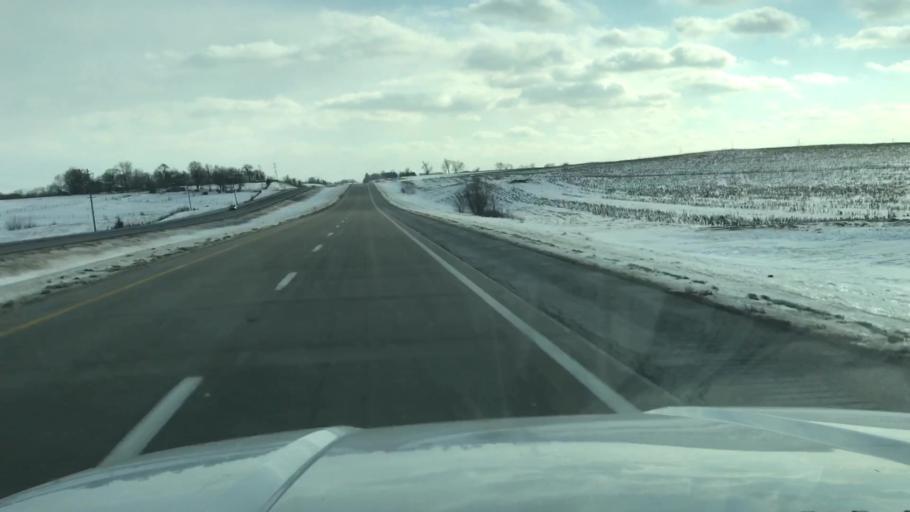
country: US
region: Missouri
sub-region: Nodaway County
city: Maryville
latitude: 40.2240
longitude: -94.8682
